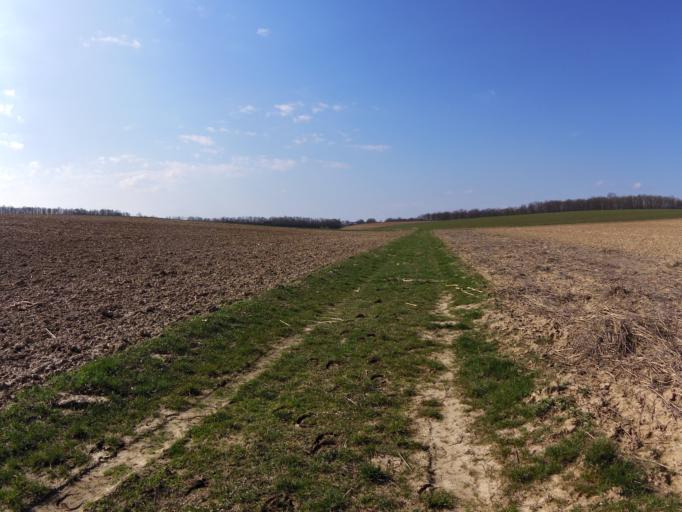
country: DE
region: Bavaria
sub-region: Regierungsbezirk Unterfranken
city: Rottendorf
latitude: 49.8001
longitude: 10.0622
